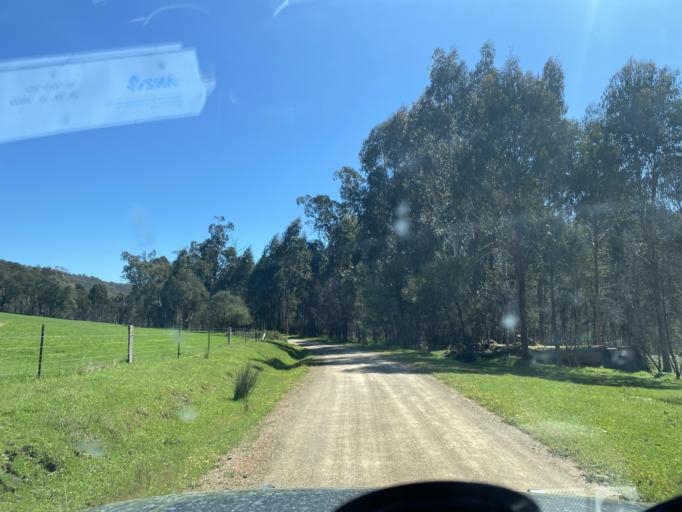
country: AU
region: Victoria
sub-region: Benalla
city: Benalla
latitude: -36.7007
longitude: 146.1788
